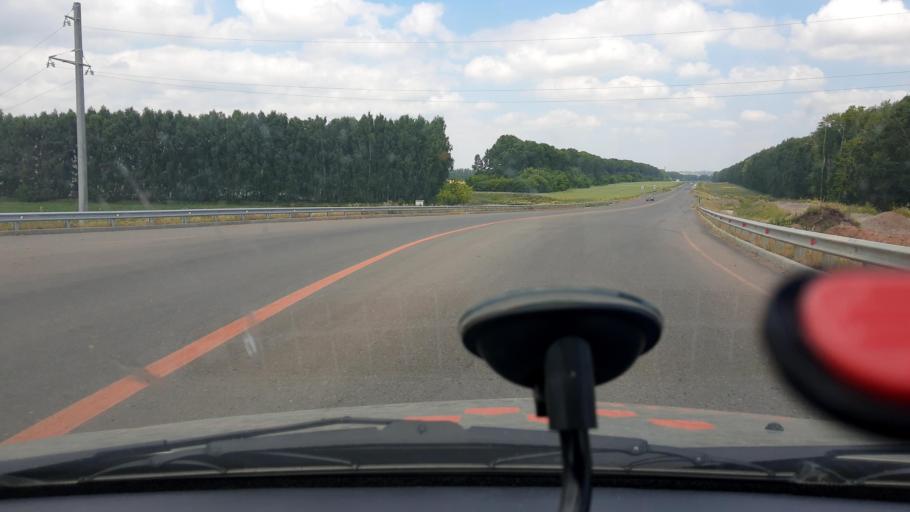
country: RU
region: Bashkortostan
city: Buzdyak
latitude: 54.6466
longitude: 54.5380
